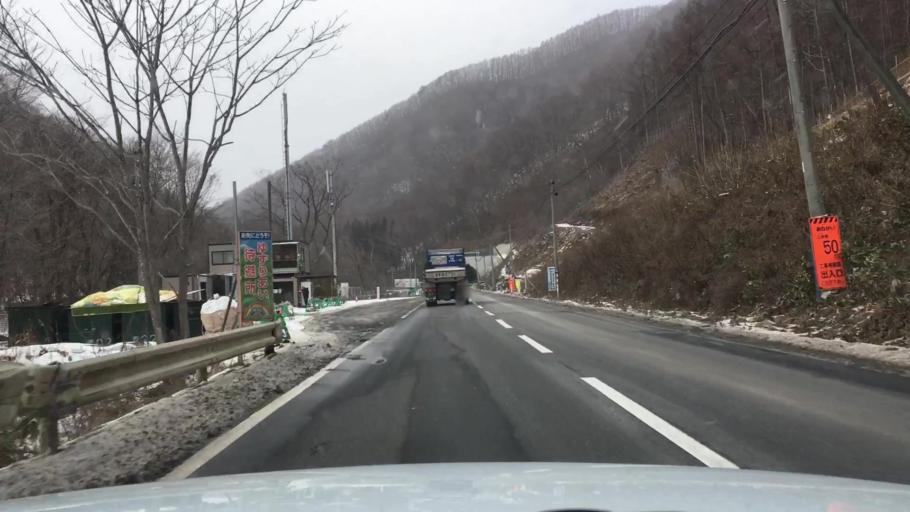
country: JP
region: Iwate
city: Tono
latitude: 39.6242
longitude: 141.4709
